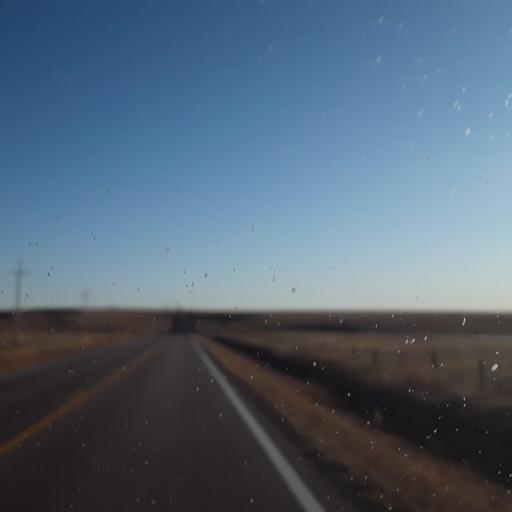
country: US
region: Kansas
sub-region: Wallace County
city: Sharon Springs
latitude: 38.9976
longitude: -101.7391
